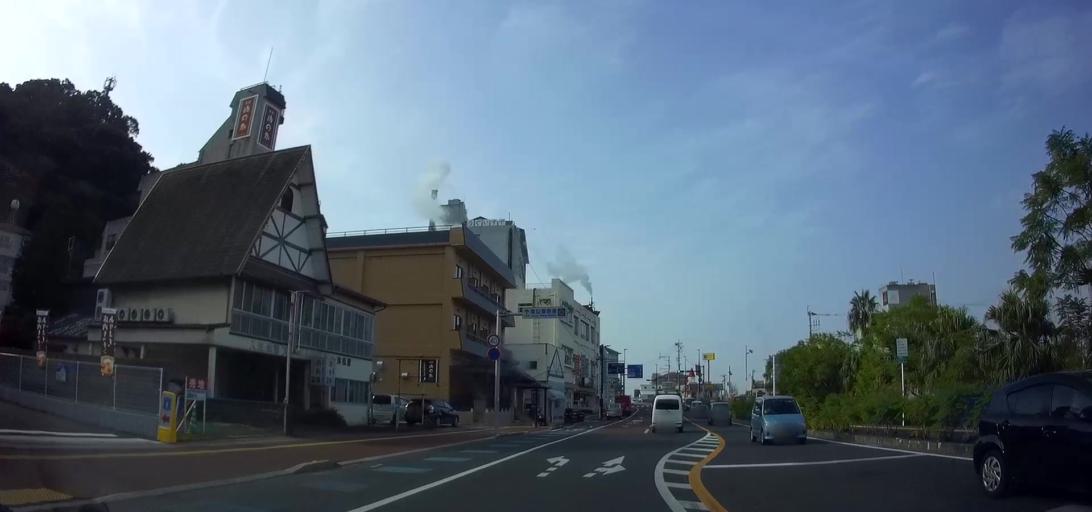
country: JP
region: Nagasaki
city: Shimabara
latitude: 32.7263
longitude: 130.2060
